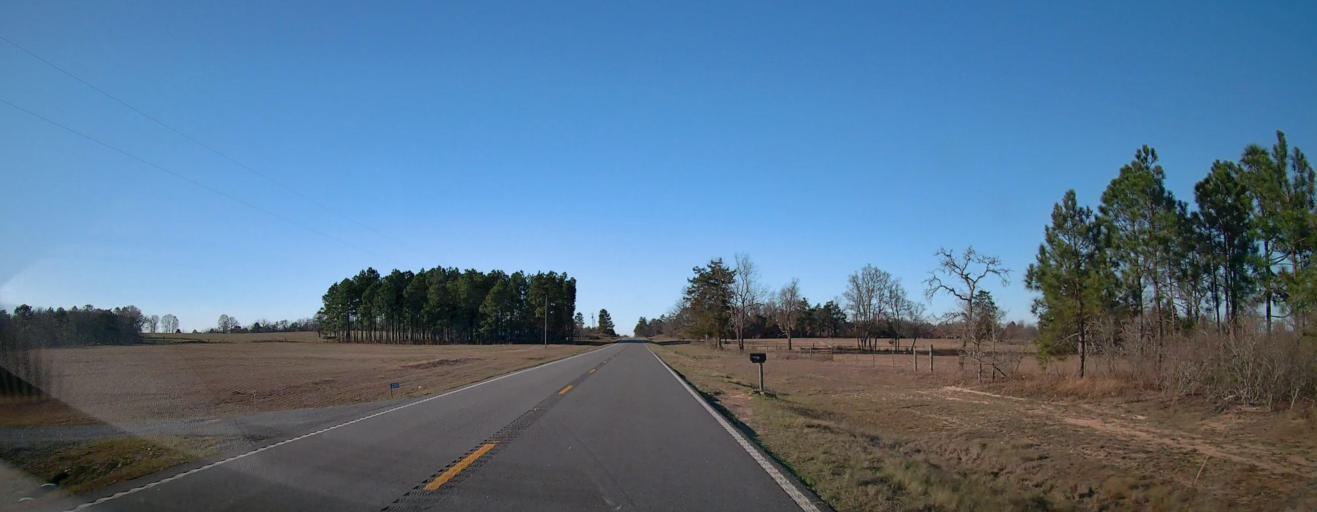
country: US
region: Georgia
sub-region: Talbot County
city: Talbotton
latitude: 32.5218
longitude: -84.4284
